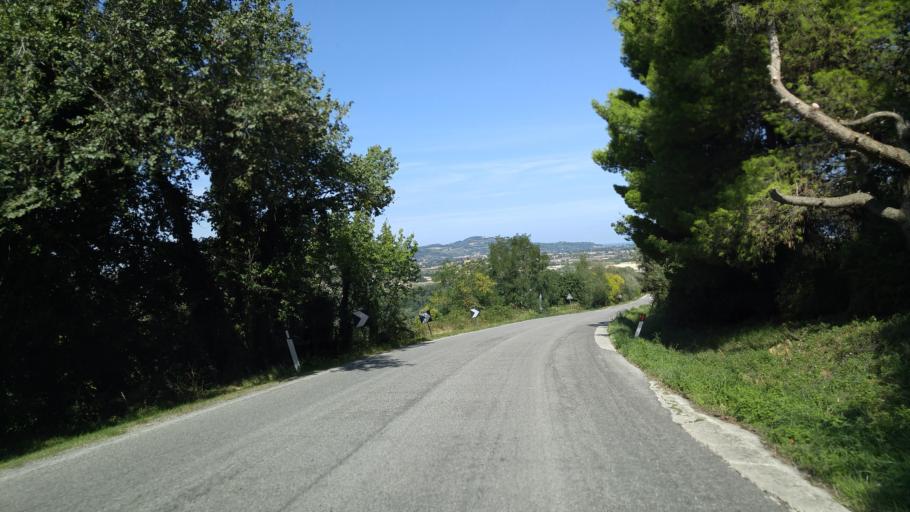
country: IT
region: The Marches
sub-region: Provincia di Pesaro e Urbino
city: Piagge
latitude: 43.7535
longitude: 12.9720
